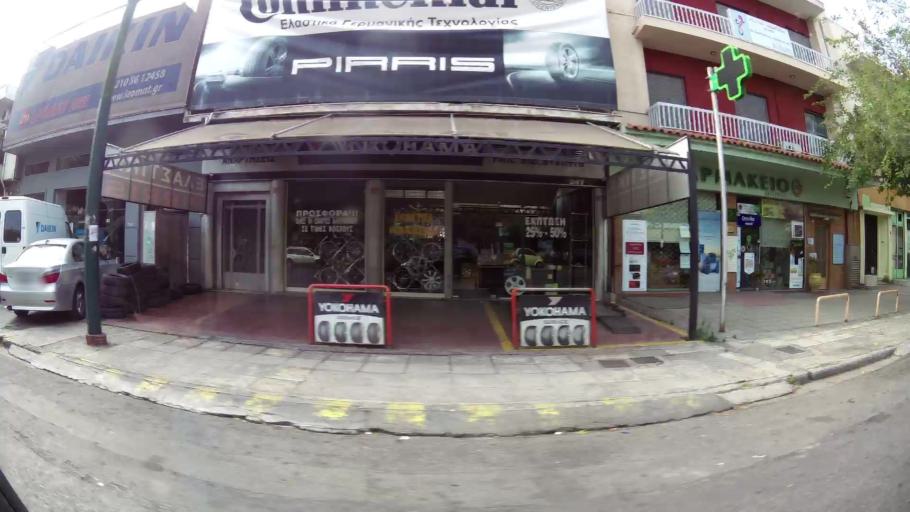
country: GR
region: Attica
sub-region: Nomarchia Athinas
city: Peristeri
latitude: 38.0009
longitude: 23.7060
